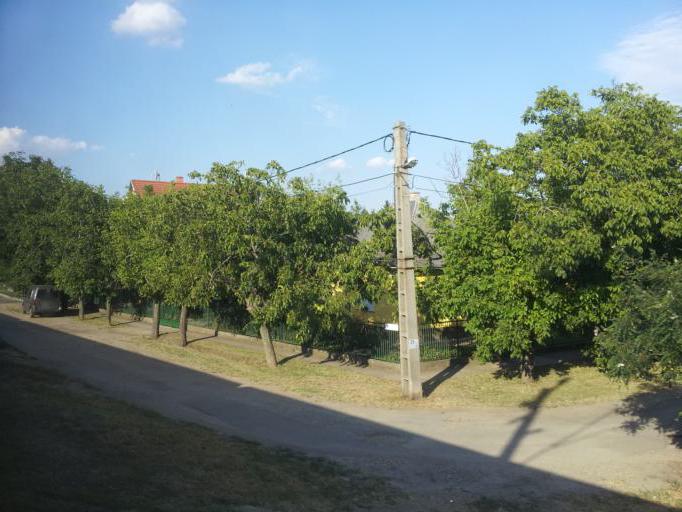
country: HU
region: Pest
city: Dunaharaszti
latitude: 47.3508
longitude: 19.0954
